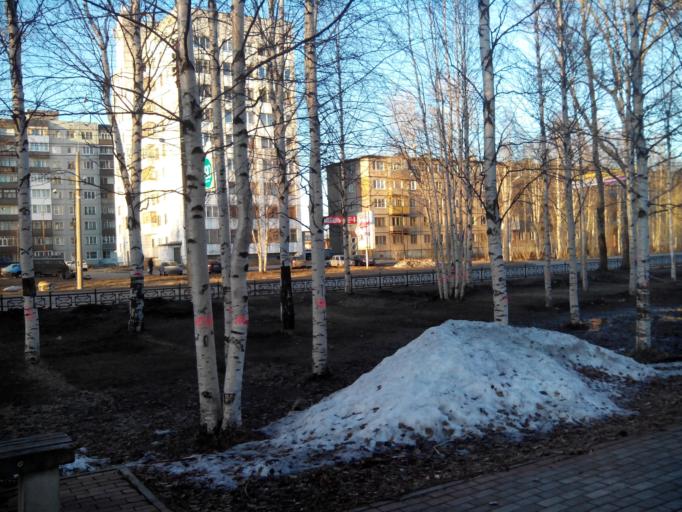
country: RU
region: Arkhangelskaya
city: Arkhangel'sk
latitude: 64.5231
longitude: 40.6122
